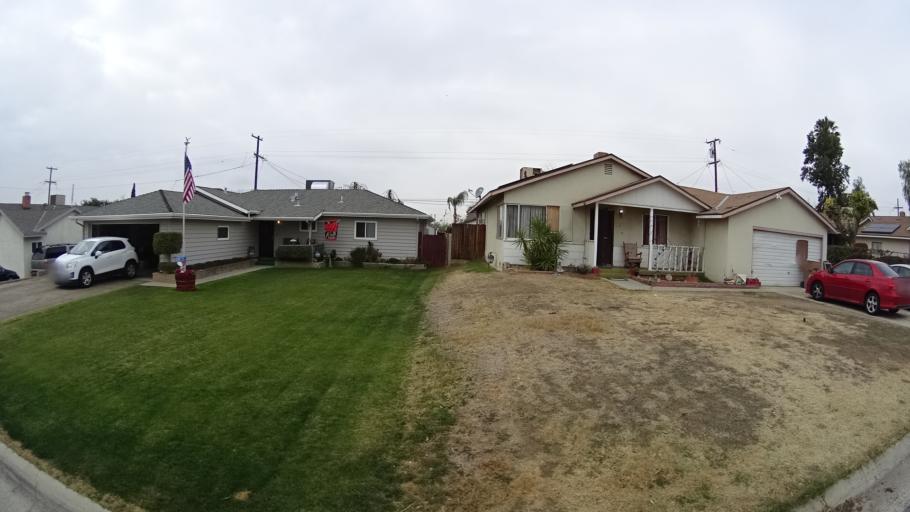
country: US
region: California
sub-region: Kern County
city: Bakersfield
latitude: 35.3784
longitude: -118.9252
